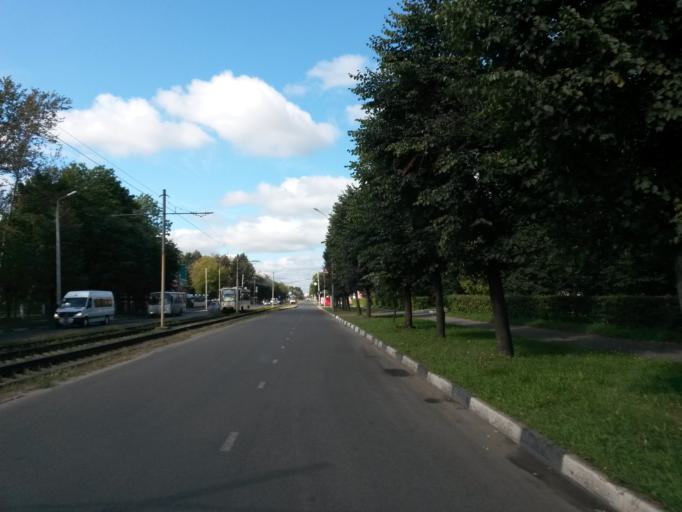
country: RU
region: Jaroslavl
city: Yaroslavl
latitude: 57.6375
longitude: 39.8522
